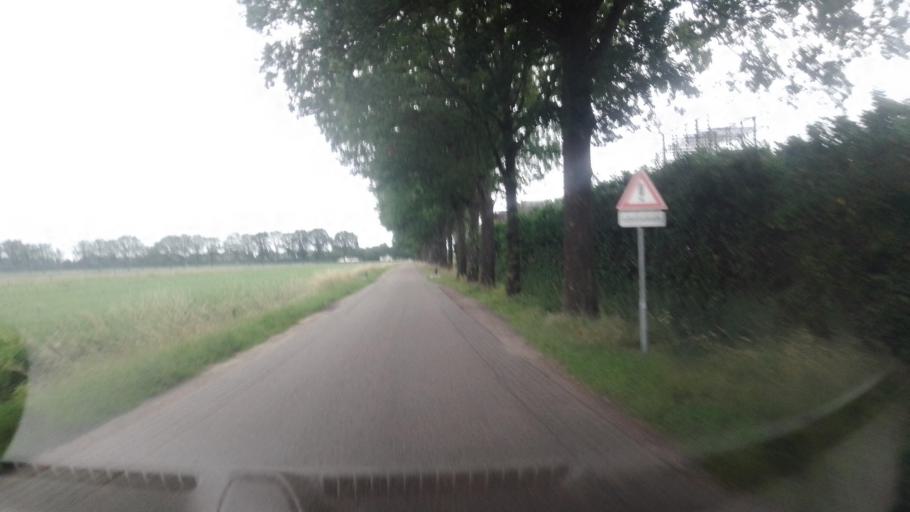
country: NL
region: Limburg
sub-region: Gemeente Beesel
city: Offenbeek
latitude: 51.2771
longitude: 6.1121
